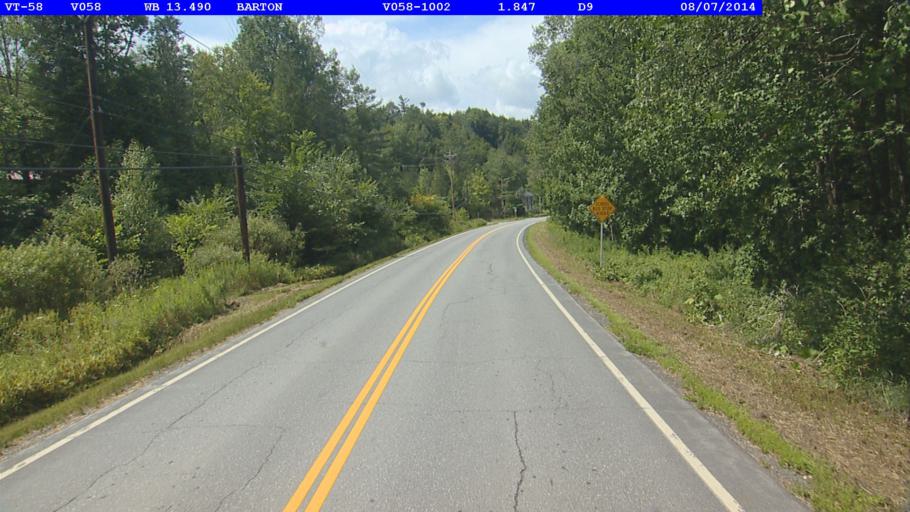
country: US
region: Vermont
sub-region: Orleans County
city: Newport
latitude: 44.8018
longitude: -72.1769
